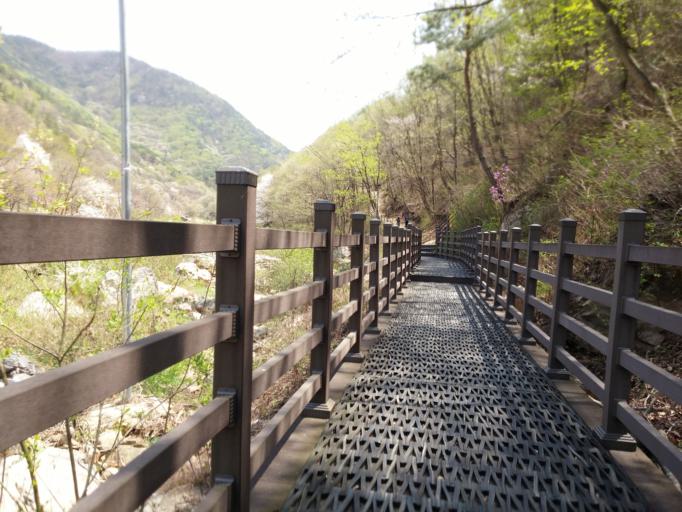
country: KR
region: Chungcheongbuk-do
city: Okcheon
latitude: 36.2384
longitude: 127.5563
